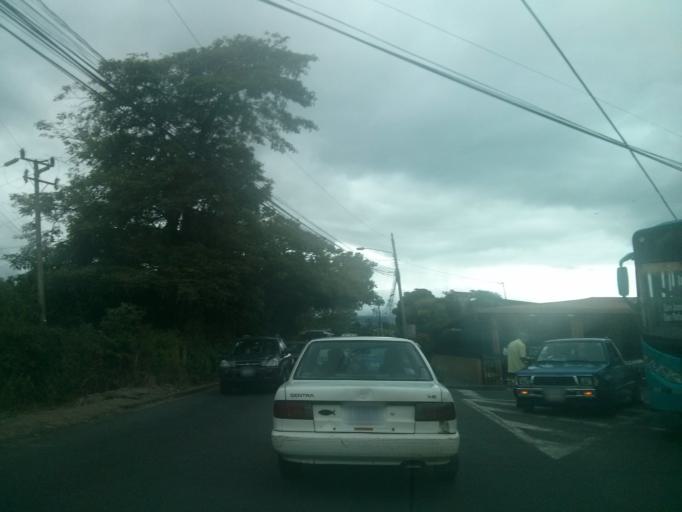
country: CR
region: Heredia
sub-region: Canton de Belen
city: San Antonio
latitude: 9.9794
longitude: -84.1943
